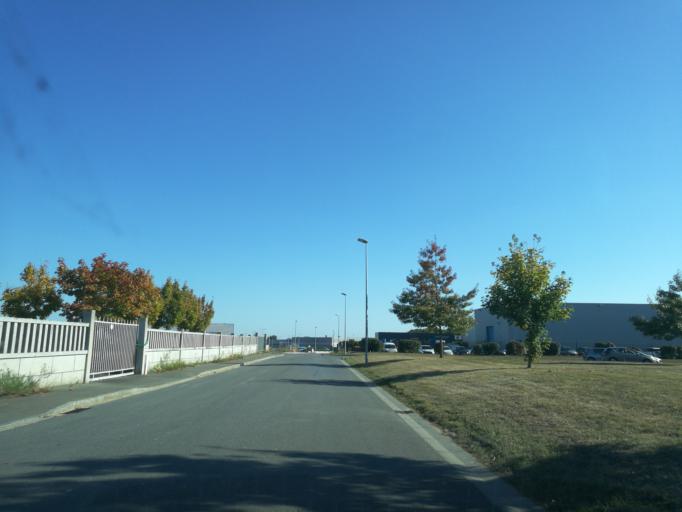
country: FR
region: Brittany
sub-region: Departement d'Ille-et-Vilaine
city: Pleumeleuc
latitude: 48.1799
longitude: -1.9256
